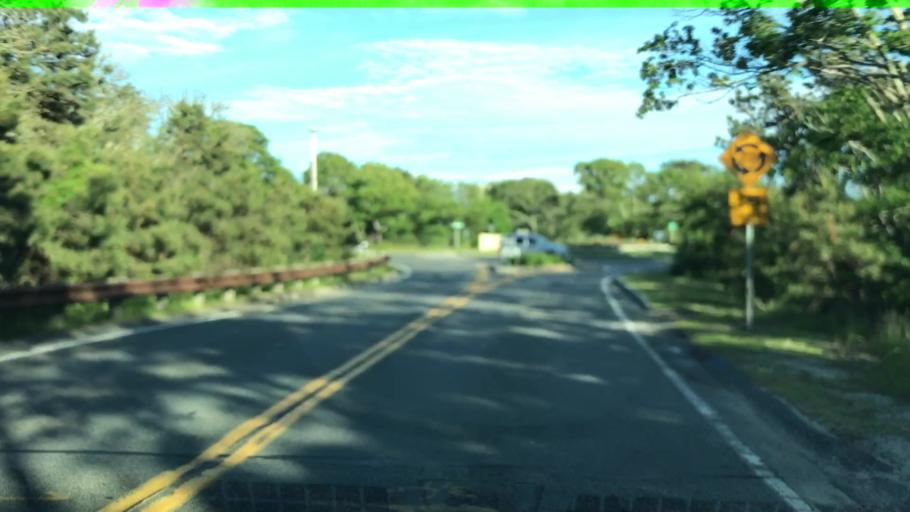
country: US
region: Massachusetts
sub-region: Barnstable County
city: East Harwich
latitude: 41.7010
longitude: -70.0321
